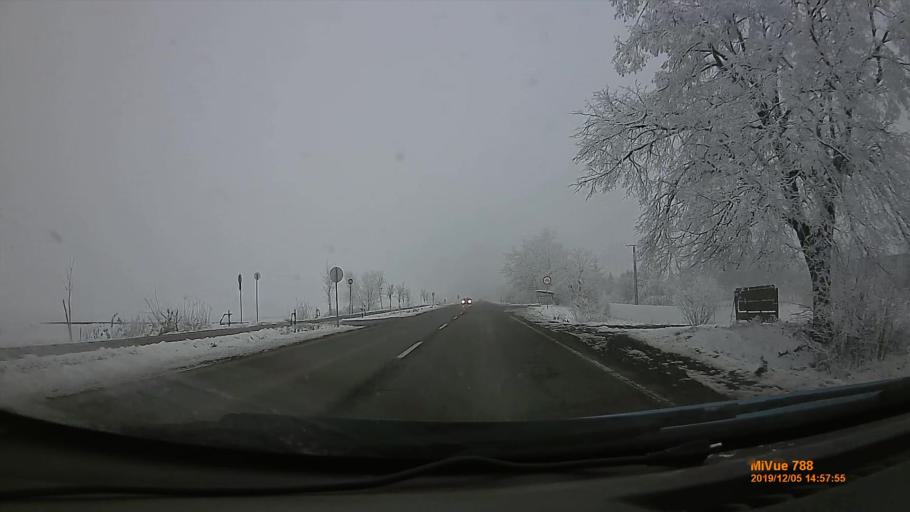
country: HU
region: Szabolcs-Szatmar-Bereg
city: Nyirtelek
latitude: 48.0436
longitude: 21.5791
